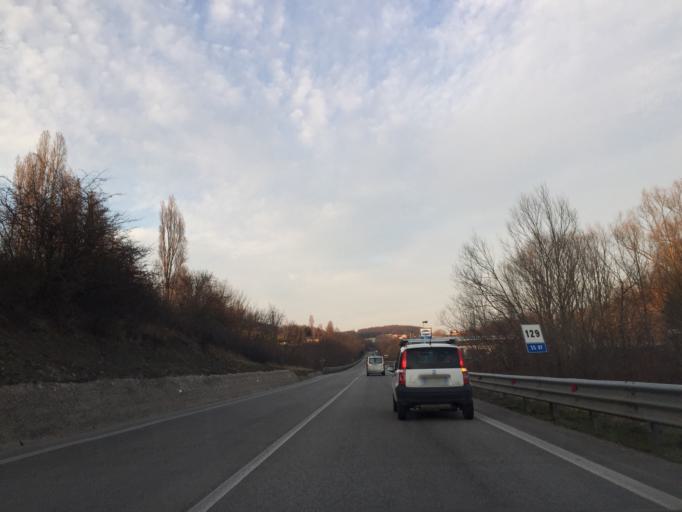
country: IT
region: Molise
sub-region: Provincia di Campobasso
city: Vinchiaturo
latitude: 41.5375
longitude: 14.6163
